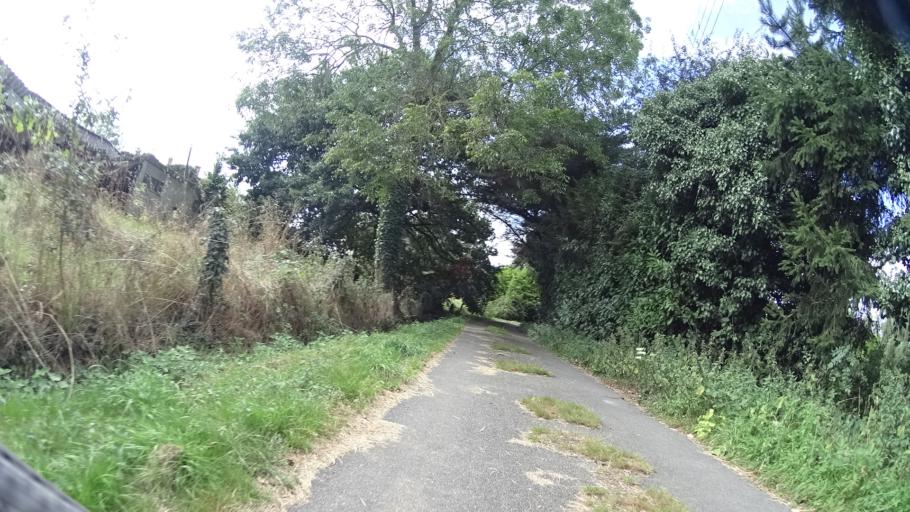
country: FR
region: Brittany
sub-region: Departement d'Ille-et-Vilaine
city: La Meziere
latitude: 48.2234
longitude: -1.7416
